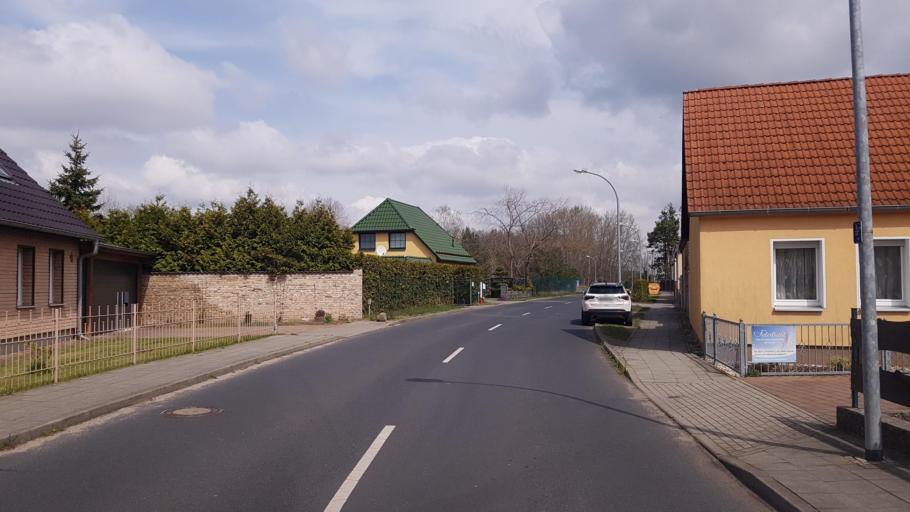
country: DE
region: Brandenburg
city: Luckenwalde
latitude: 52.1156
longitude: 13.1966
